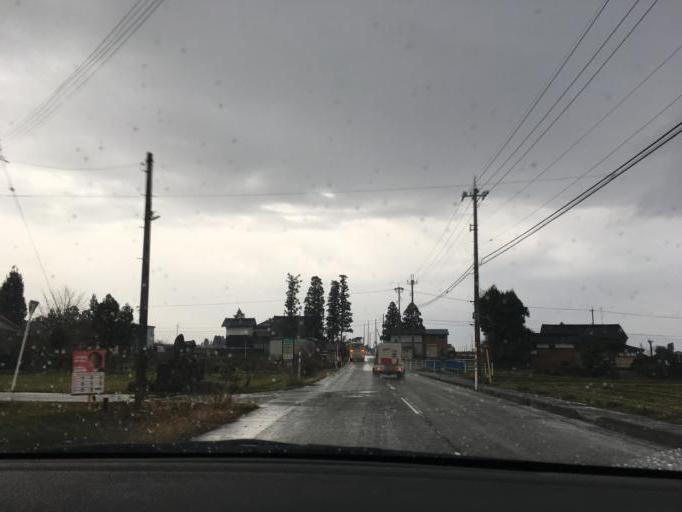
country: JP
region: Toyama
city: Nanto-shi
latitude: 36.5525
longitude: 136.9464
